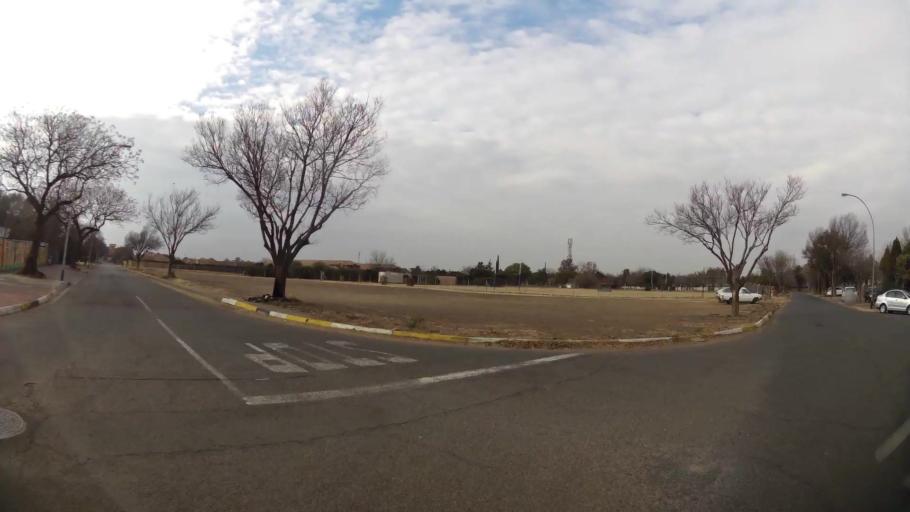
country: ZA
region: Orange Free State
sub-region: Mangaung Metropolitan Municipality
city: Bloemfontein
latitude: -29.1204
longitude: 26.1851
